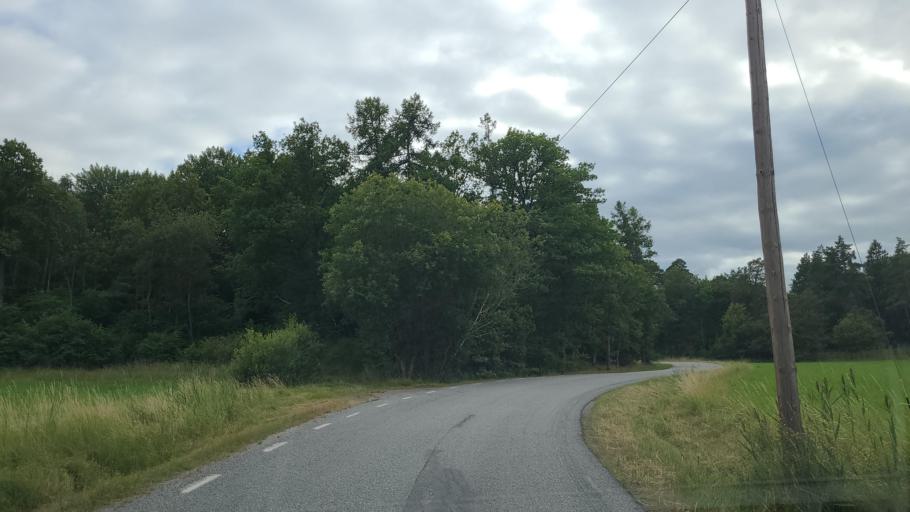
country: SE
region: Stockholm
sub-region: Upplands-Bro Kommun
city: Bro
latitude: 59.4720
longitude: 17.5942
